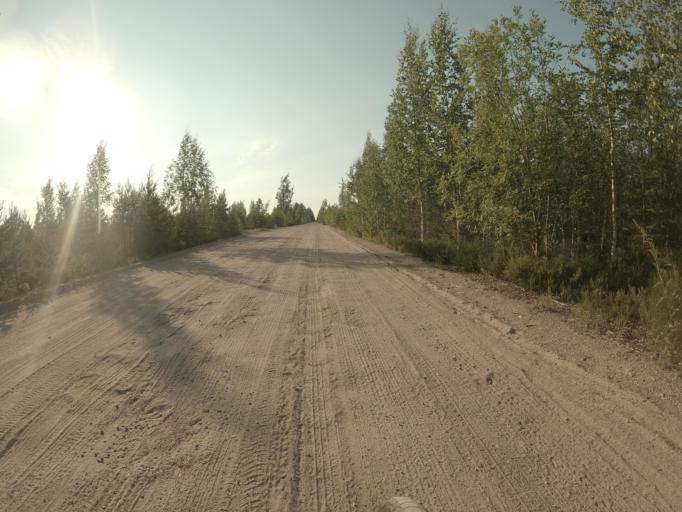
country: RU
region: Leningrad
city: Yakovlevo
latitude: 60.4522
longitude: 29.2564
